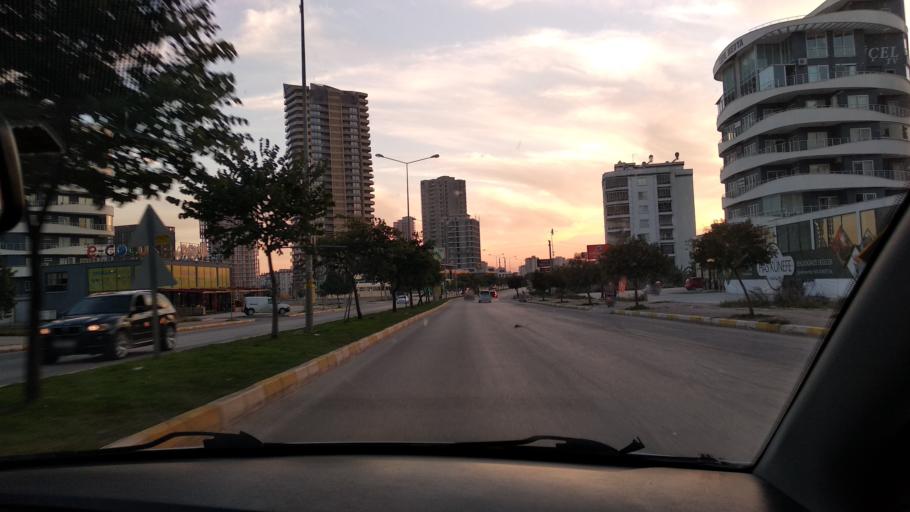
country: TR
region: Mersin
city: Mercin
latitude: 36.8021
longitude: 34.5837
